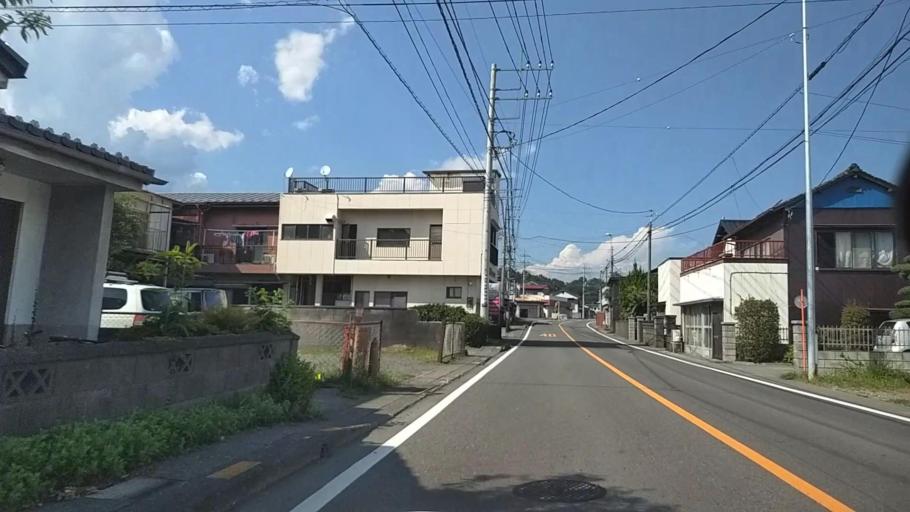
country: JP
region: Yamanashi
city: Ryuo
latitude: 35.4093
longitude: 138.4423
